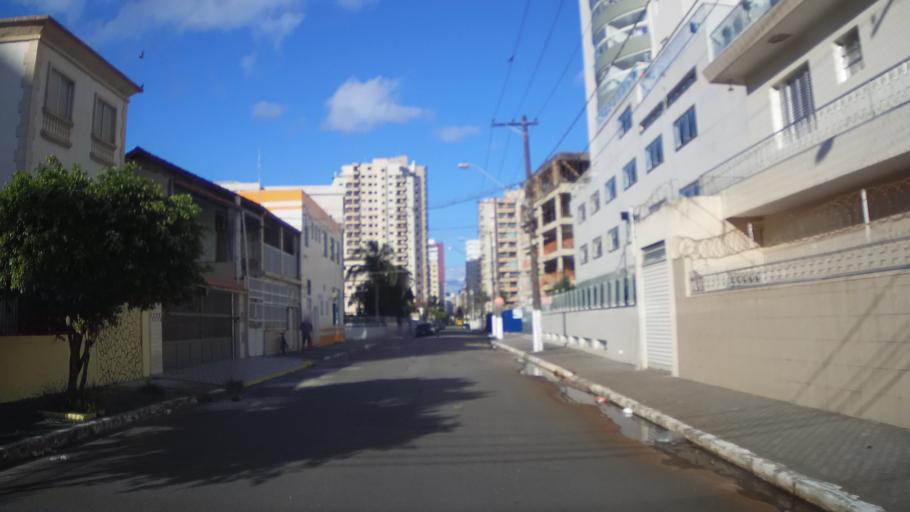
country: BR
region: Sao Paulo
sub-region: Praia Grande
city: Praia Grande
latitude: -24.0206
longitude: -46.4524
